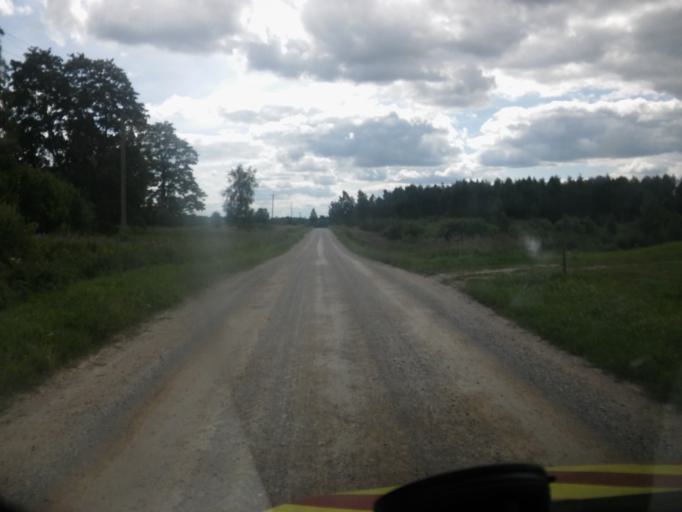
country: EE
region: Viljandimaa
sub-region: Karksi vald
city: Karksi-Nuia
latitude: 58.1007
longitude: 25.5030
